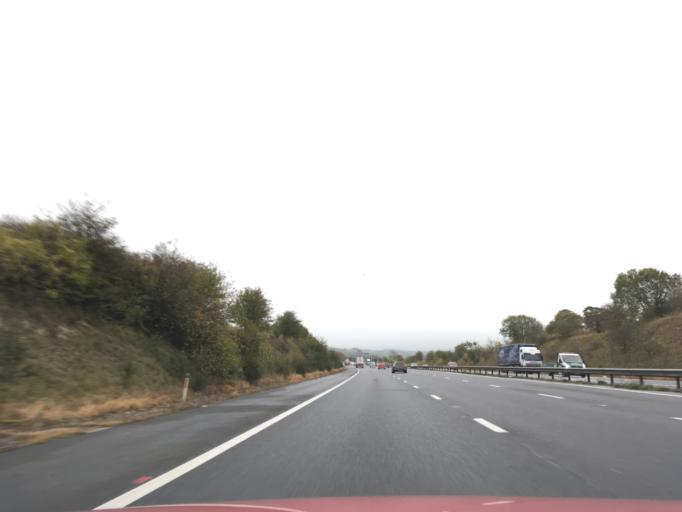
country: GB
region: England
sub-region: Borough of Swindon
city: Bishopstone
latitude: 51.5200
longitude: -1.6625
